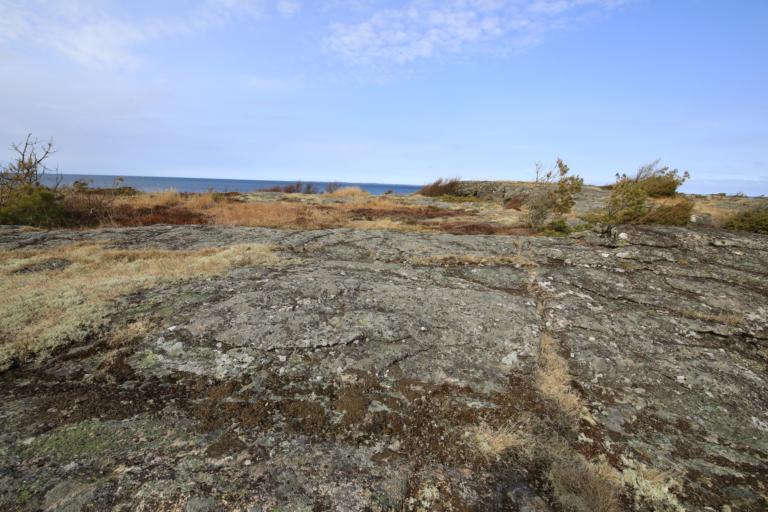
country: SE
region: Halland
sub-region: Kungsbacka Kommun
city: Frillesas
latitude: 57.2569
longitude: 12.0980
